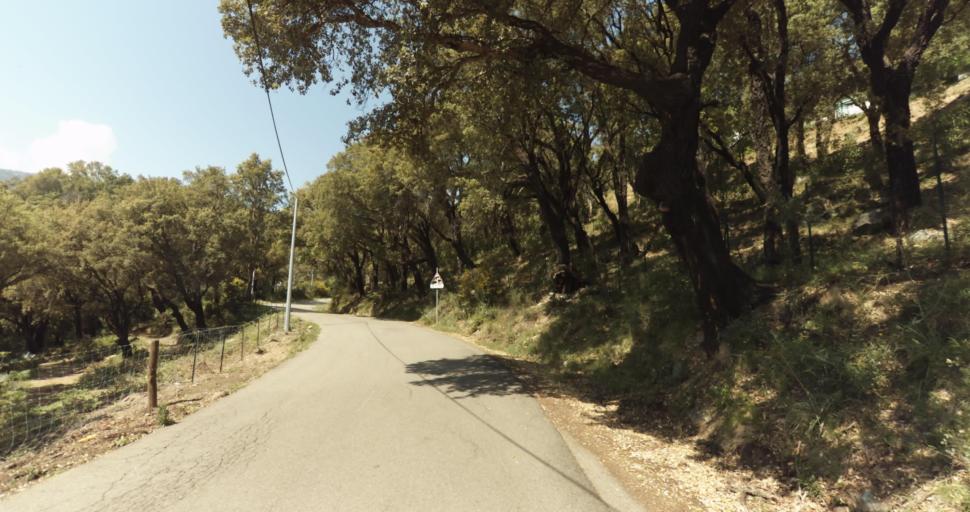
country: FR
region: Corsica
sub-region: Departement de la Haute-Corse
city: Biguglia
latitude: 42.6133
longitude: 9.4154
